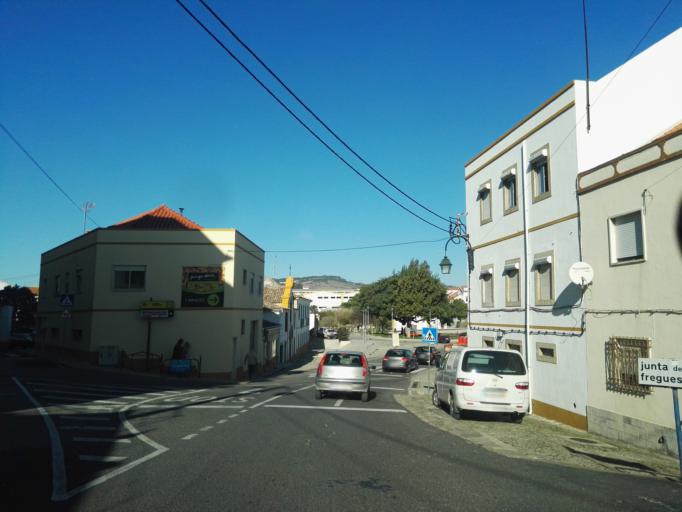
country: PT
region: Lisbon
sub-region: Arruda Dos Vinhos
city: Arruda dos Vinhos
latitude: 38.9856
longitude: -9.0779
